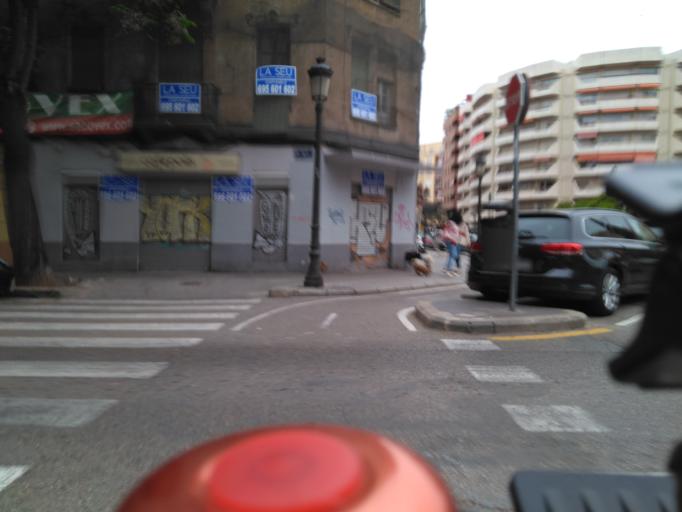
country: ES
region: Valencia
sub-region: Provincia de Valencia
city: Valencia
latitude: 39.4721
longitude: -0.3903
